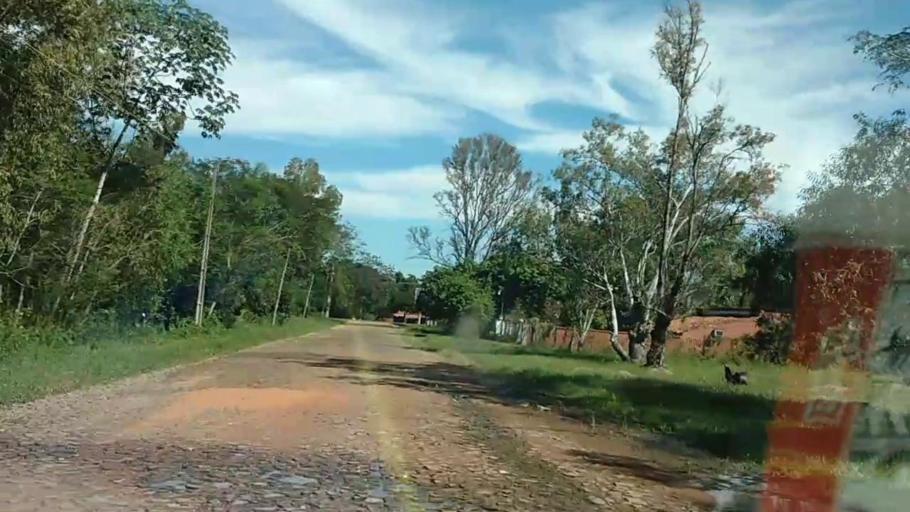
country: PY
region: Cordillera
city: San Bernardino
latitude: -25.3326
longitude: -57.2724
